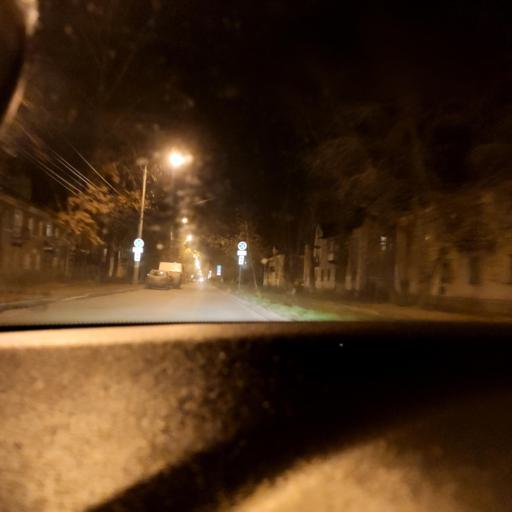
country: RU
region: Samara
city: Samara
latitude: 53.2205
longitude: 50.2558
